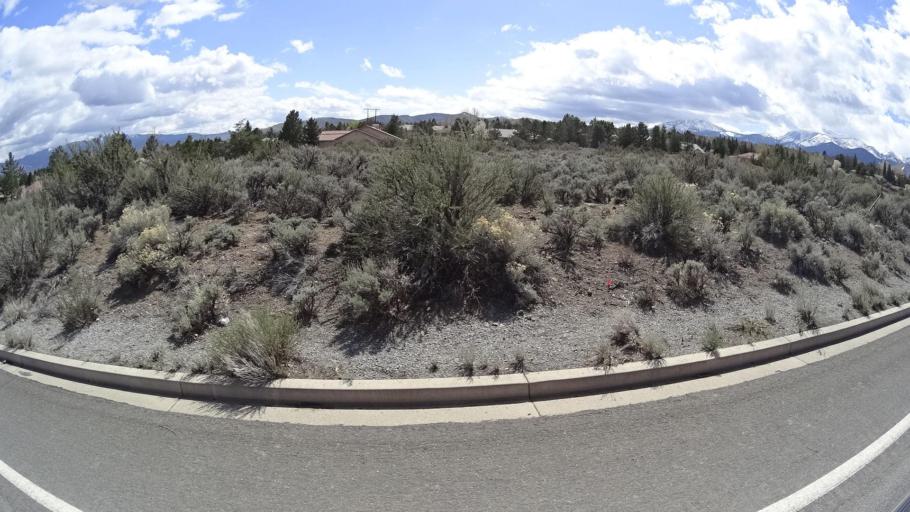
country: US
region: Nevada
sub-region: Washoe County
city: Reno
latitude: 39.4187
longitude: -119.7827
